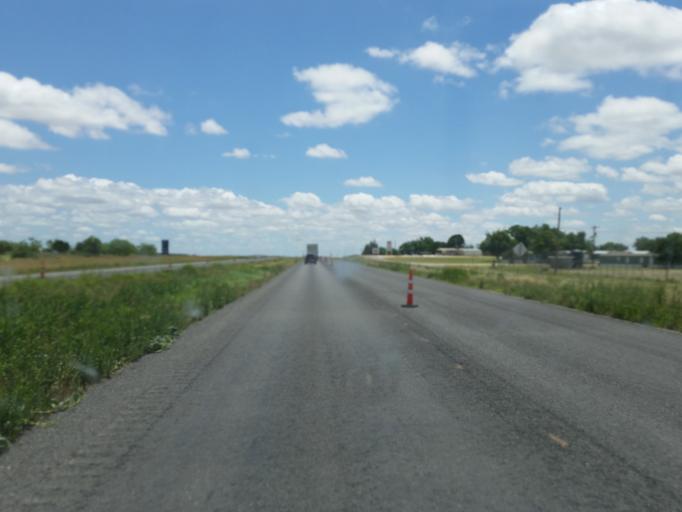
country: US
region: Texas
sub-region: Scurry County
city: Snyder
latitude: 32.7256
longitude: -100.8920
